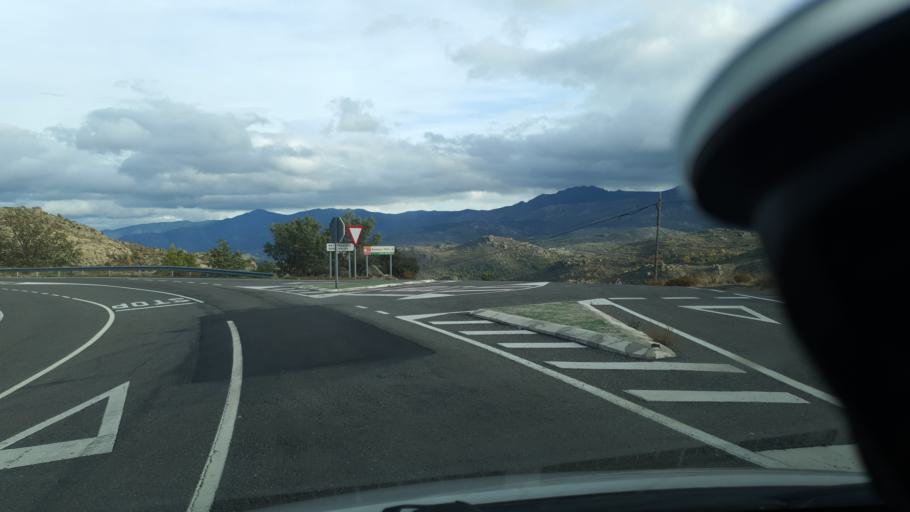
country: ES
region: Castille and Leon
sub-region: Provincia de Avila
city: Navalosa
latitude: 40.3955
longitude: -4.9226
